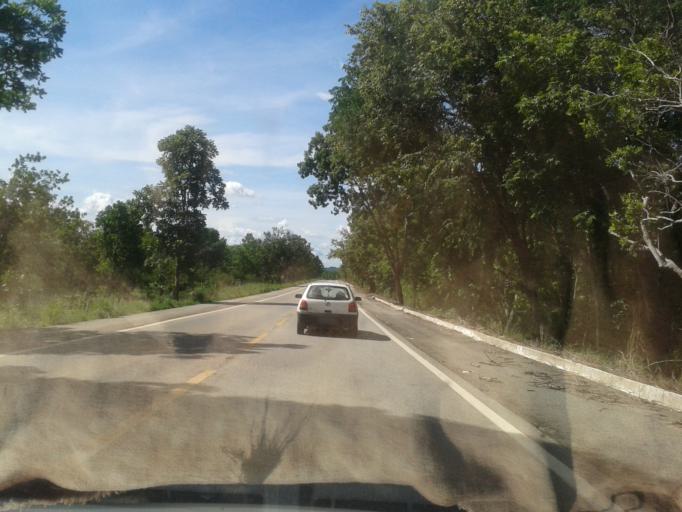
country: BR
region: Goias
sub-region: Itapuranga
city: Itapuranga
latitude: -15.3677
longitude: -50.3903
